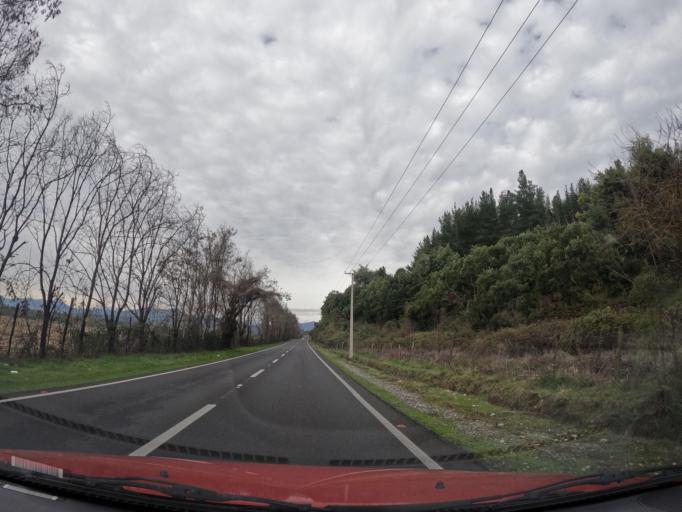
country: CL
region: Maule
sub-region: Provincia de Linares
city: Linares
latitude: -35.9134
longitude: -71.4775
